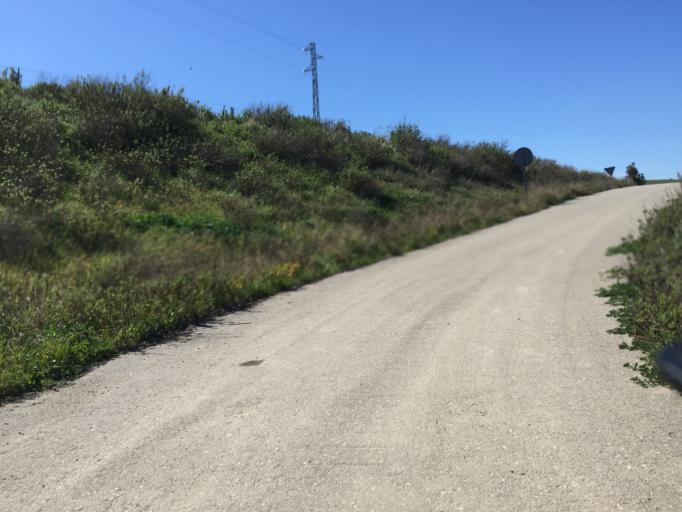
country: ES
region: Andalusia
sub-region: Provincia de Cadiz
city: Vejer de la Frontera
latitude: 36.2565
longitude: -5.9781
